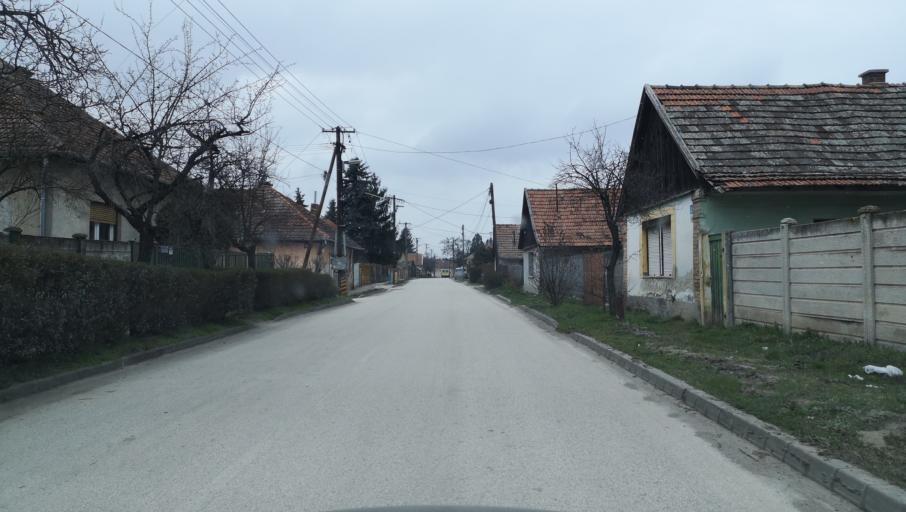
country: HU
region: Pest
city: Monor
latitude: 47.3555
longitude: 19.4478
